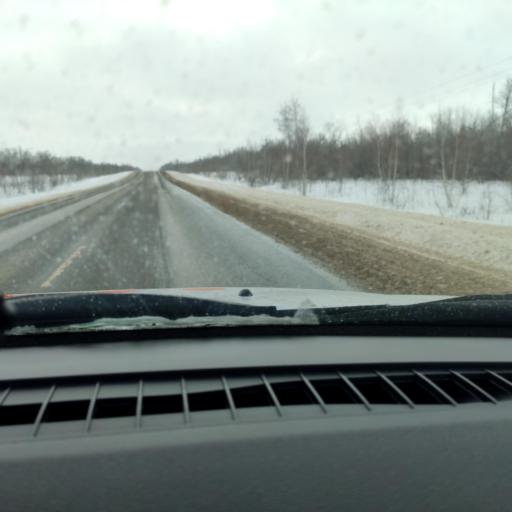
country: RU
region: Samara
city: Dubovyy Umet
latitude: 52.7587
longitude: 50.4930
